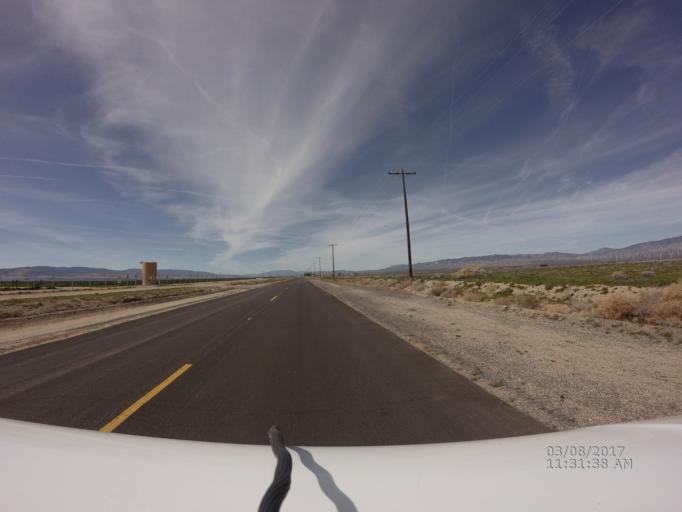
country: US
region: California
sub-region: Los Angeles County
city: Green Valley
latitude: 34.8192
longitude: -118.3859
